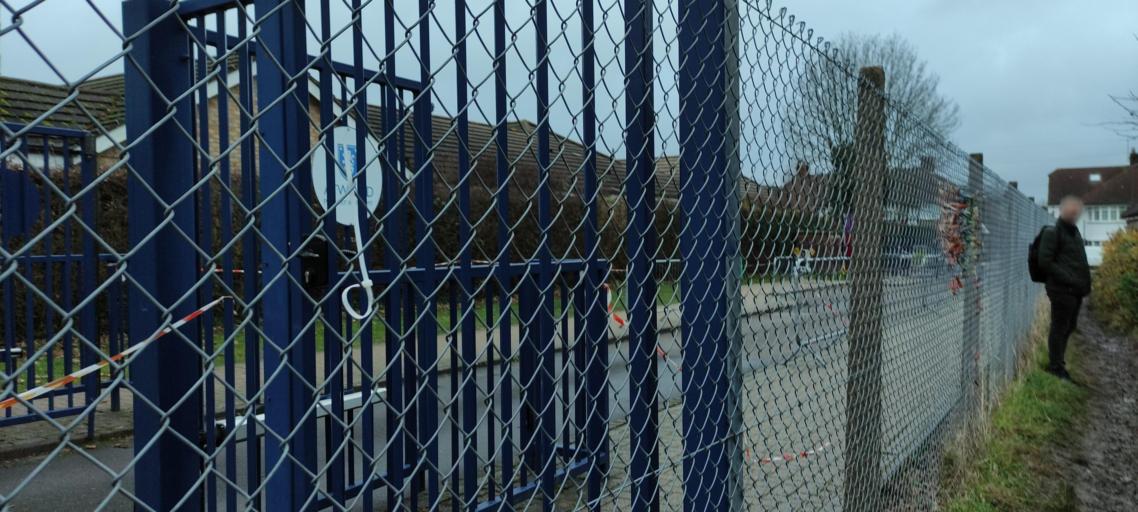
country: GB
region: England
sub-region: Greater London
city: Whyteleafe
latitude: 51.3281
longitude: -0.0740
